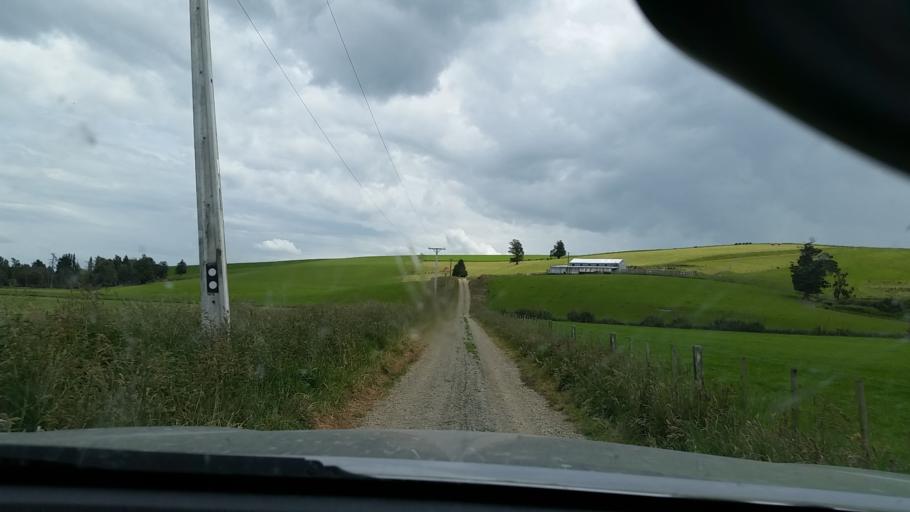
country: NZ
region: Southland
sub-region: Southland District
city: Winton
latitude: -46.0215
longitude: 168.3046
